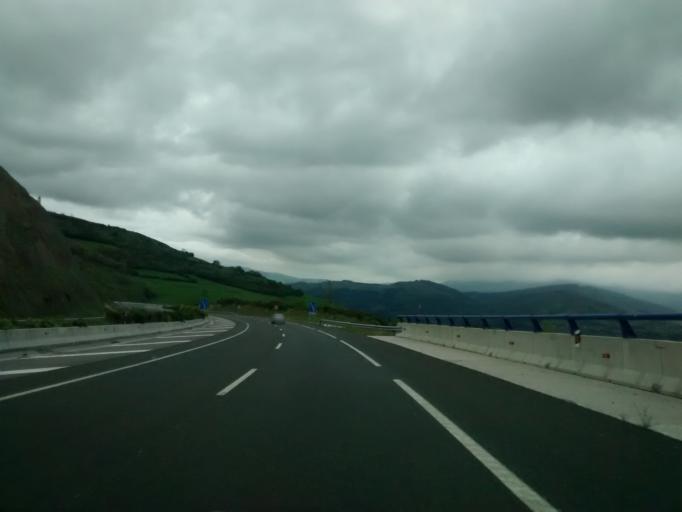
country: ES
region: Cantabria
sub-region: Provincia de Cantabria
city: Barcena de Pie de Concha
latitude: 43.1321
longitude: -4.0688
